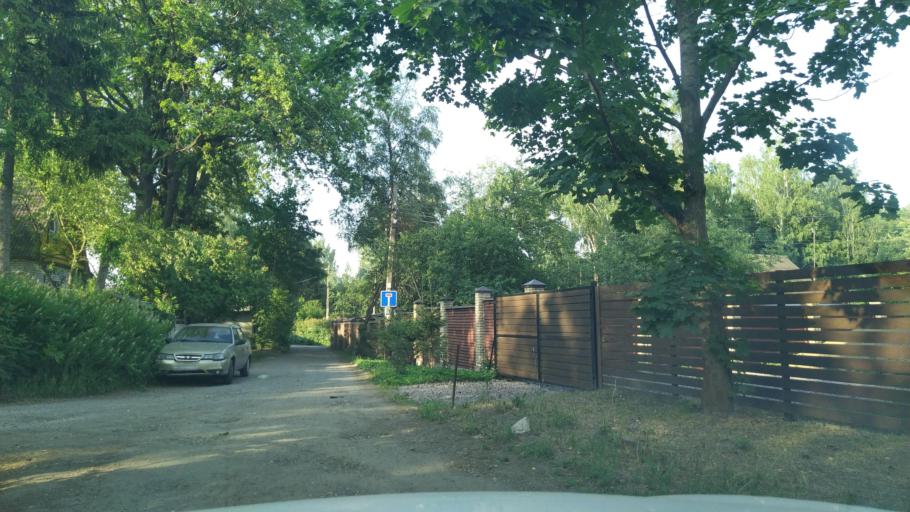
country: RU
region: Leningrad
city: Koltushi
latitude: 59.8951
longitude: 30.7331
